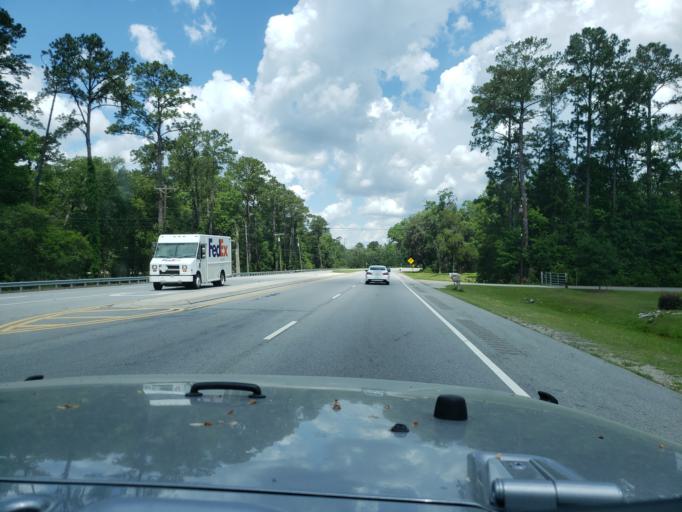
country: US
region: Georgia
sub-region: Chatham County
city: Georgetown
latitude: 32.0445
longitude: -81.2125
